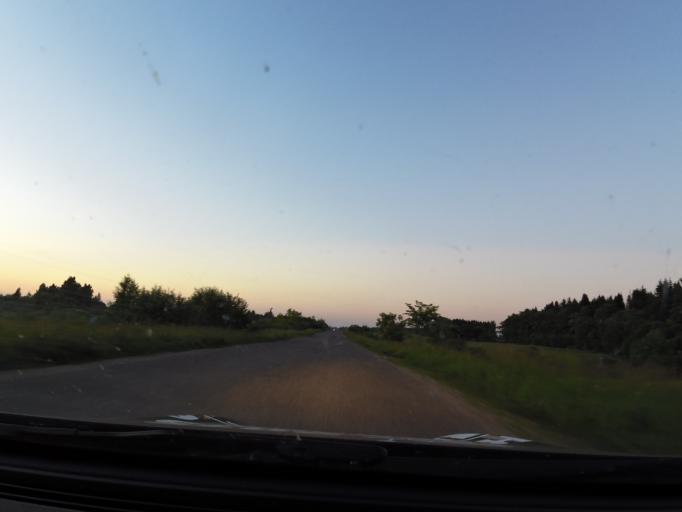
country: RU
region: Kostroma
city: Buy
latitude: 58.4619
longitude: 41.4050
